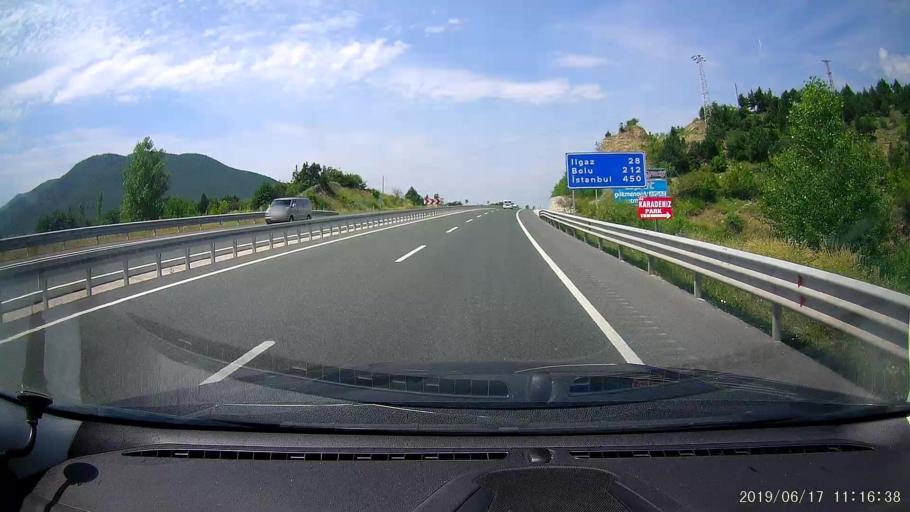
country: TR
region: Kastamonu
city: Tosya
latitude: 40.9439
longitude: 33.8951
